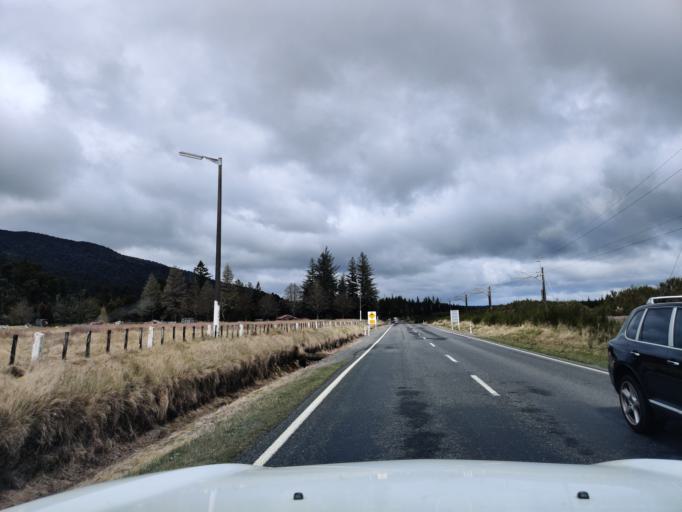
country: NZ
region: Manawatu-Wanganui
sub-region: Ruapehu District
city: Waiouru
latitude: -39.2119
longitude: 175.4016
